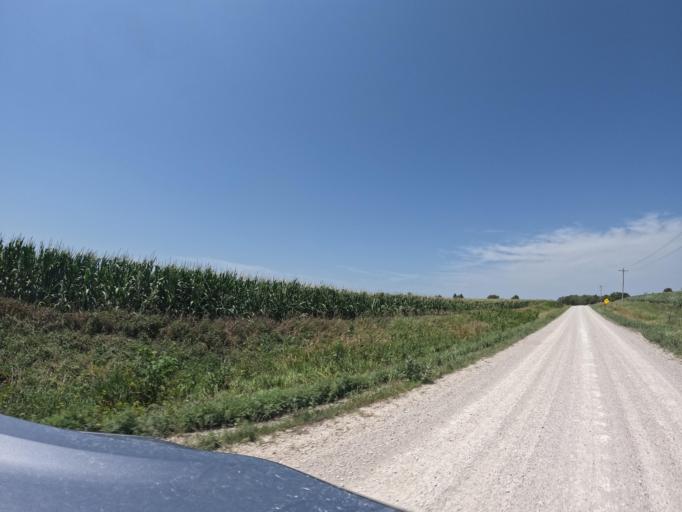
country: US
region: Iowa
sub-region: Henry County
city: Mount Pleasant
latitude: 40.9494
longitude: -91.6604
